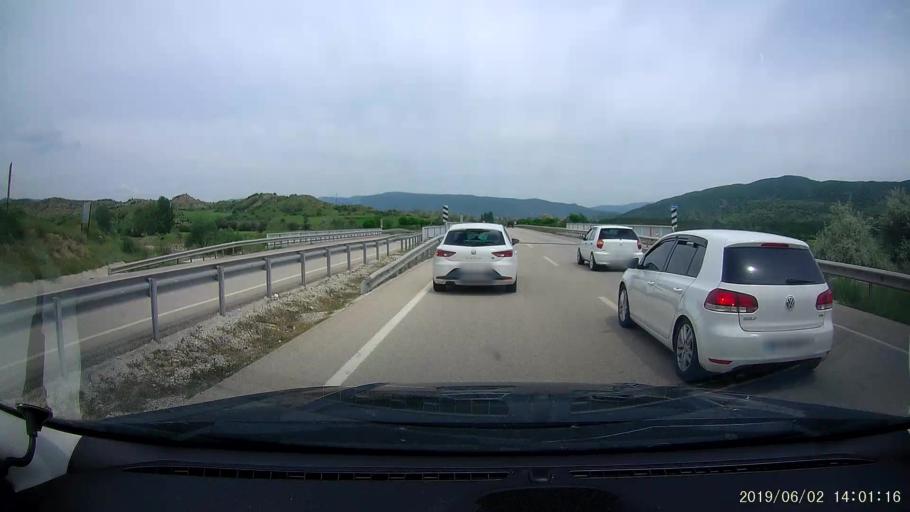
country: TR
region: Cankiri
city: Ilgaz
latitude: 40.9078
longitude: 33.5919
